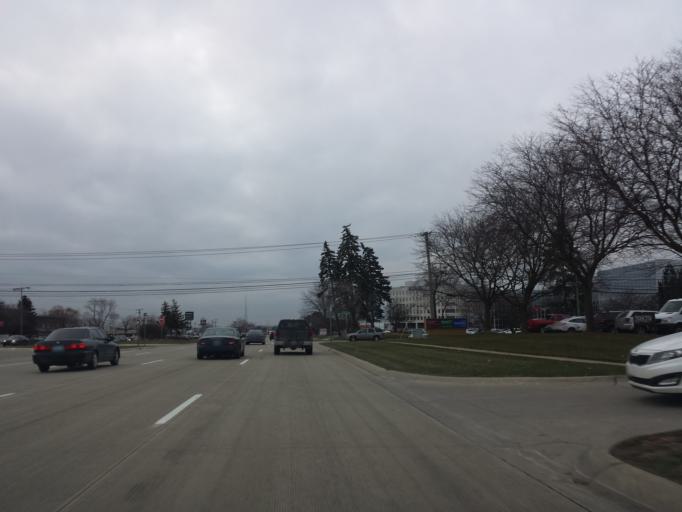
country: US
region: Michigan
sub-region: Oakland County
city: Bingham Farms
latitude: 42.5072
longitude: -83.2857
